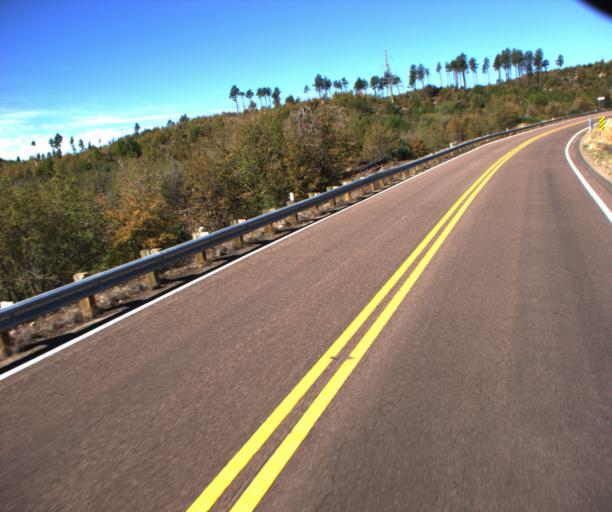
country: US
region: Arizona
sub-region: Yavapai County
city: Prescott
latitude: 34.4940
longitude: -112.4933
